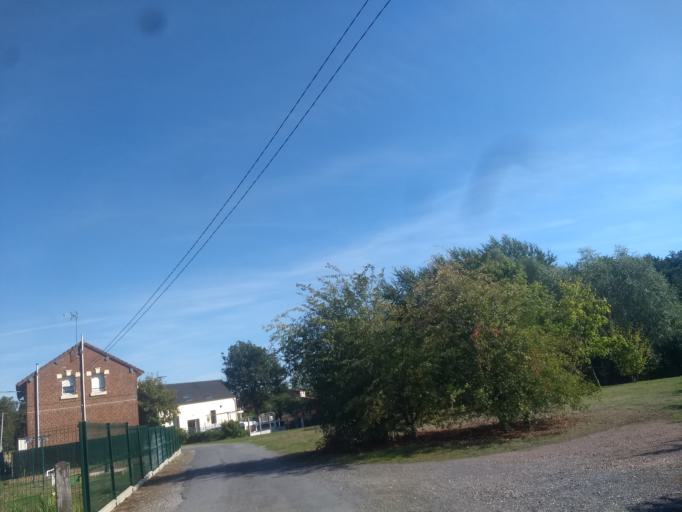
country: FR
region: Nord-Pas-de-Calais
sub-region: Departement du Pas-de-Calais
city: Fampoux
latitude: 50.2984
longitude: 2.8675
